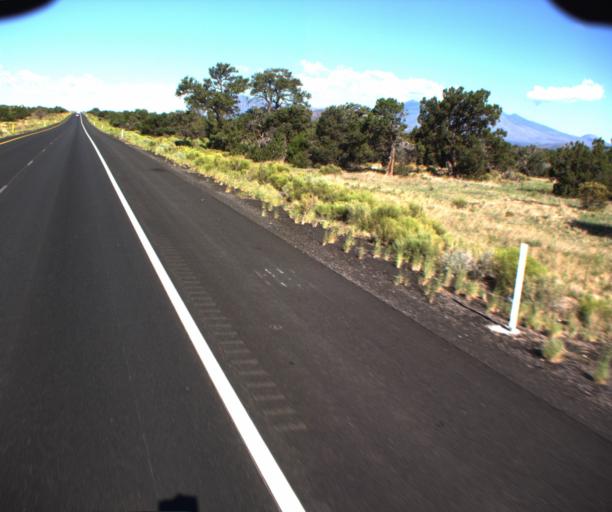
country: US
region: Arizona
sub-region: Coconino County
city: Flagstaff
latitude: 35.2020
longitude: -111.4346
